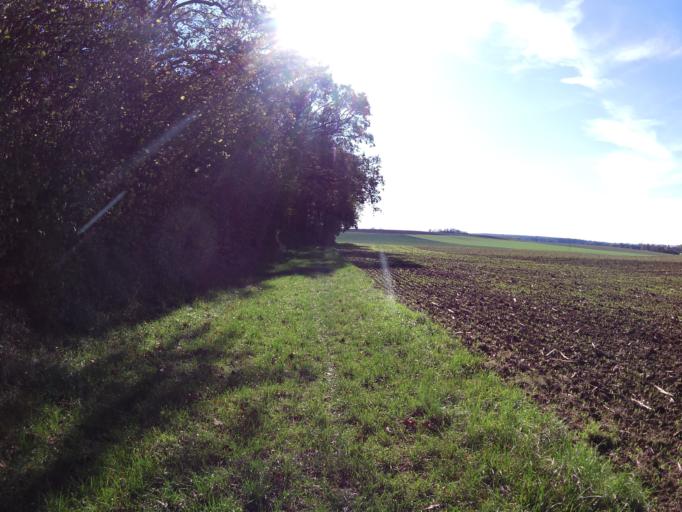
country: DE
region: Bavaria
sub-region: Regierungsbezirk Unterfranken
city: Sulzfeld am Main
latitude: 49.7130
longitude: 10.0937
